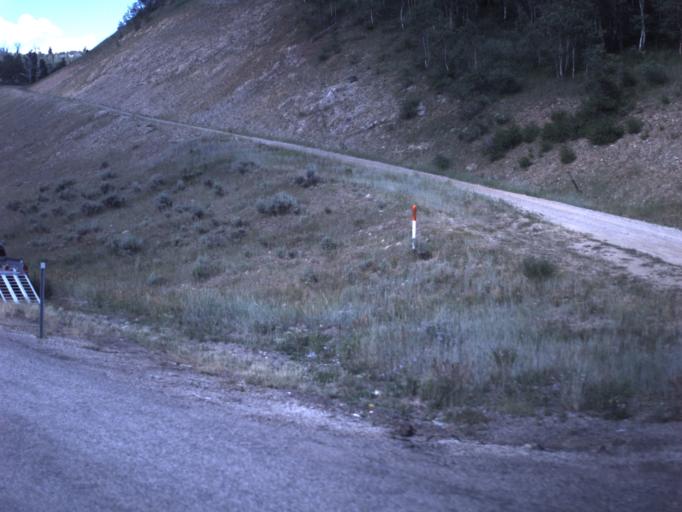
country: US
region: Utah
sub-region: Wasatch County
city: Heber
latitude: 40.3135
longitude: -111.2571
